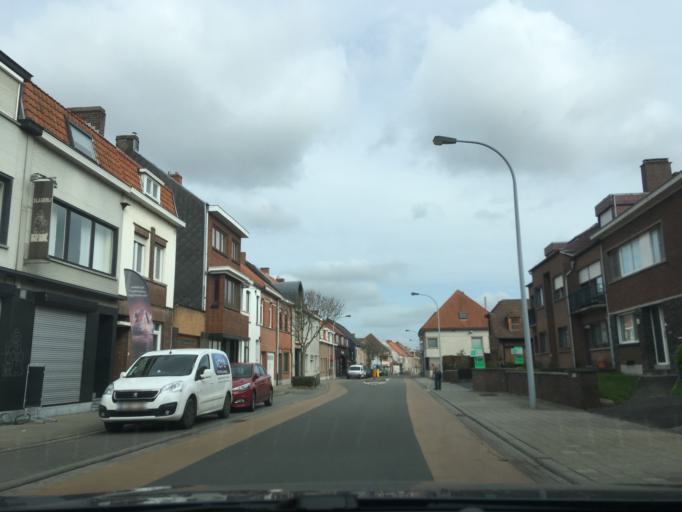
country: BE
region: Flanders
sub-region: Provincie West-Vlaanderen
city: Kortrijk
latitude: 50.8397
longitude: 3.2572
